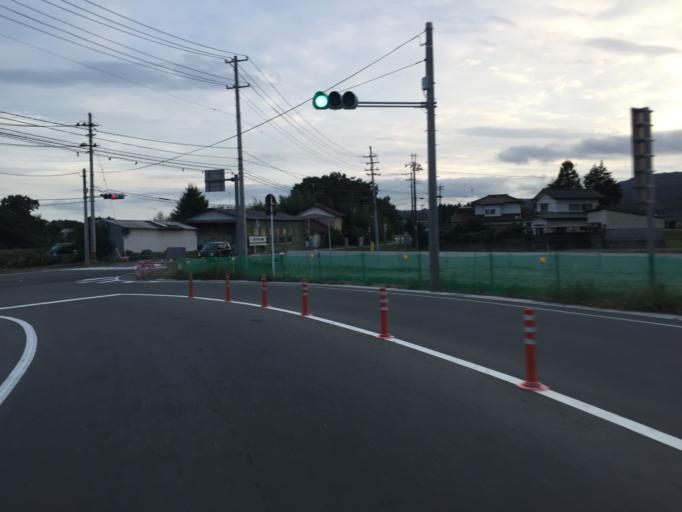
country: JP
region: Miyagi
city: Marumori
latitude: 37.7829
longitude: 140.8990
